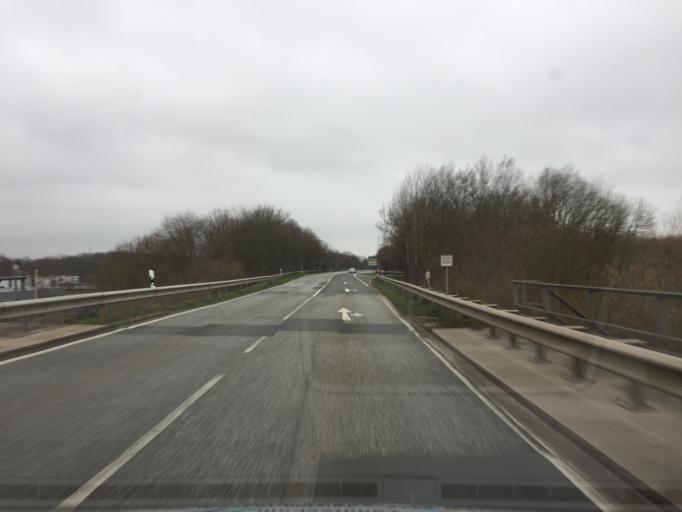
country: DE
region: North Rhine-Westphalia
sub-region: Regierungsbezirk Detmold
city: Petershagen
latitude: 52.3757
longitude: 9.0007
